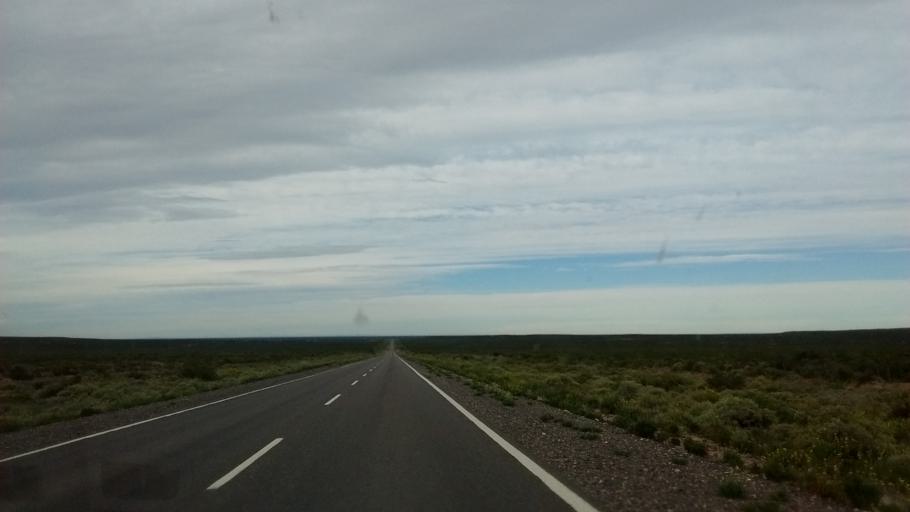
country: AR
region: Rio Negro
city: Contraalmirante Cordero
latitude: -38.4210
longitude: -68.0356
